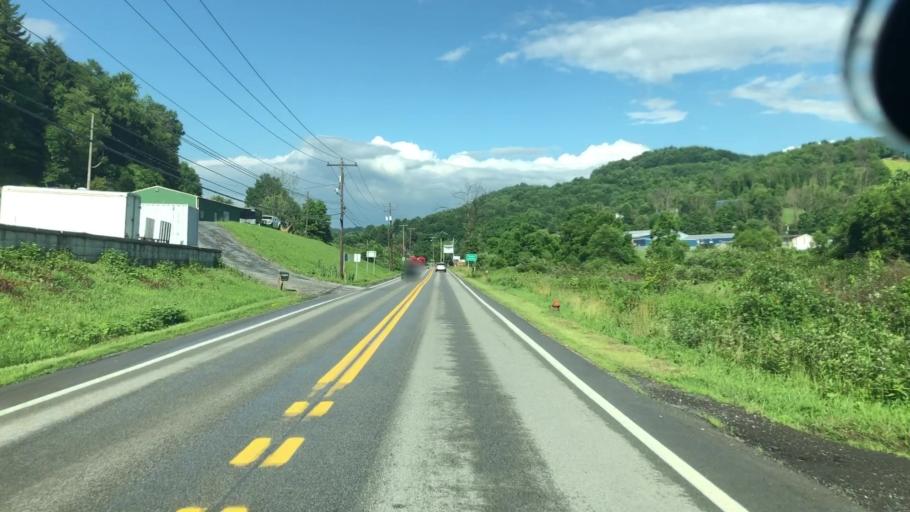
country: US
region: West Virginia
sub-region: Harrison County
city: Bridgeport
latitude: 39.2983
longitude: -80.2027
